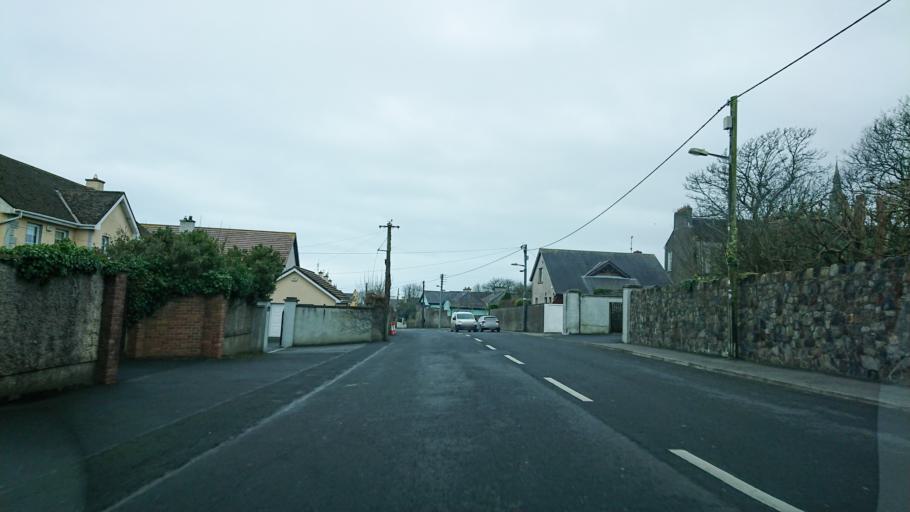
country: IE
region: Munster
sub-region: Waterford
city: Tra Mhor
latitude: 52.1646
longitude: -7.1533
